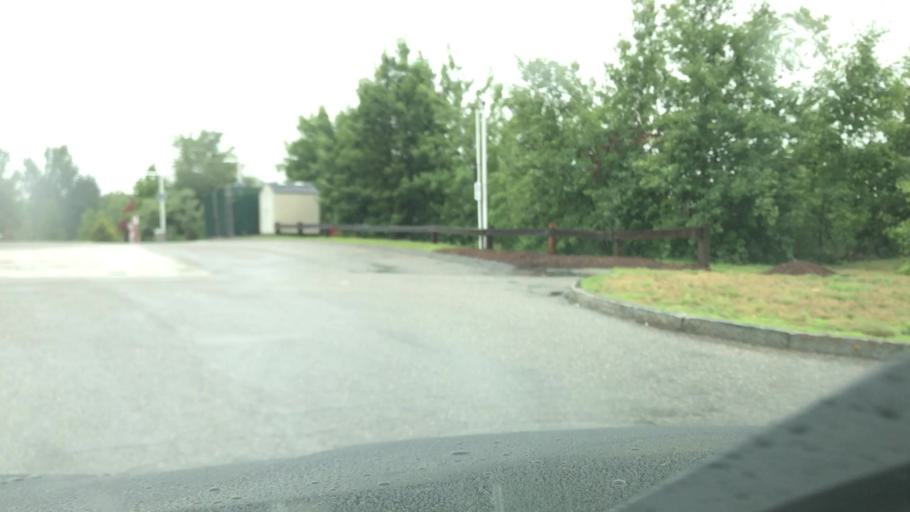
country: US
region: New Hampshire
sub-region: Strafford County
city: Somersworth
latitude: 43.2360
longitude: -70.8820
